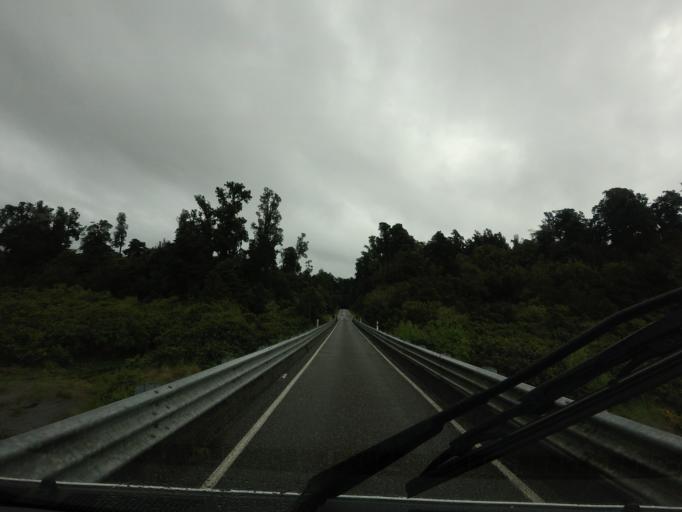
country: NZ
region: West Coast
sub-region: Westland District
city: Hokitika
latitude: -42.9807
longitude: 170.6845
